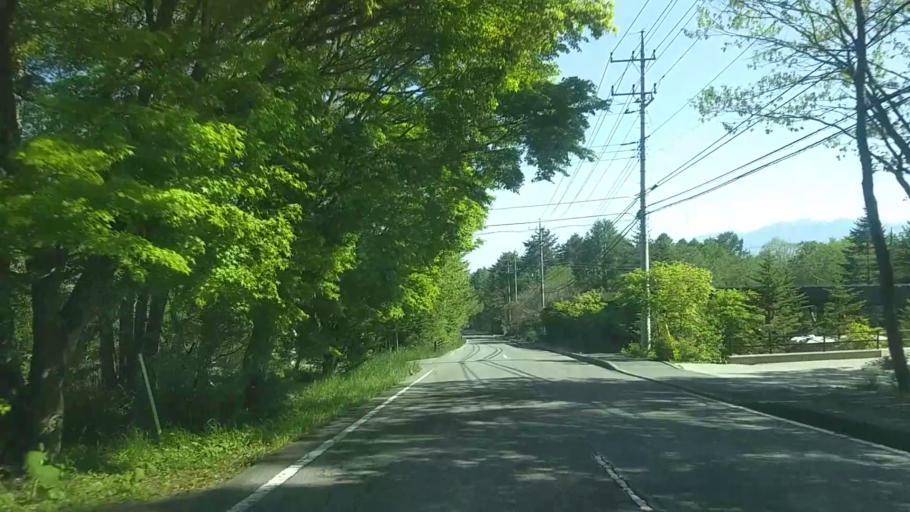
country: JP
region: Yamanashi
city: Nirasaki
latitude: 35.9121
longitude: 138.4082
